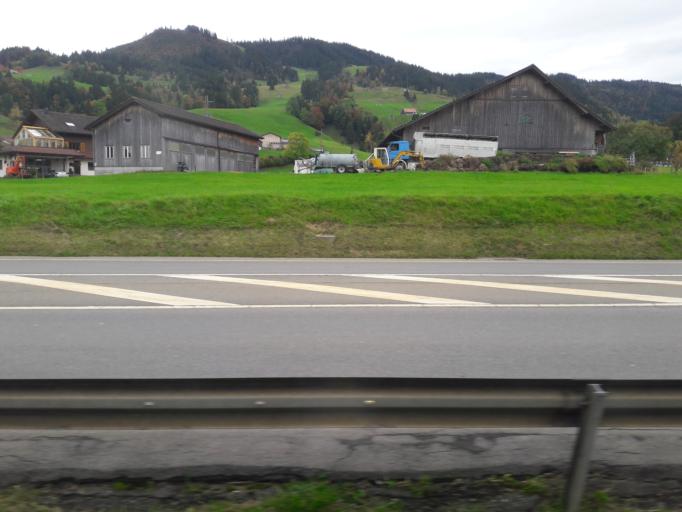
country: CH
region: Schwyz
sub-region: Bezirk Schwyz
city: Rothenthurm
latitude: 47.0944
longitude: 8.6702
